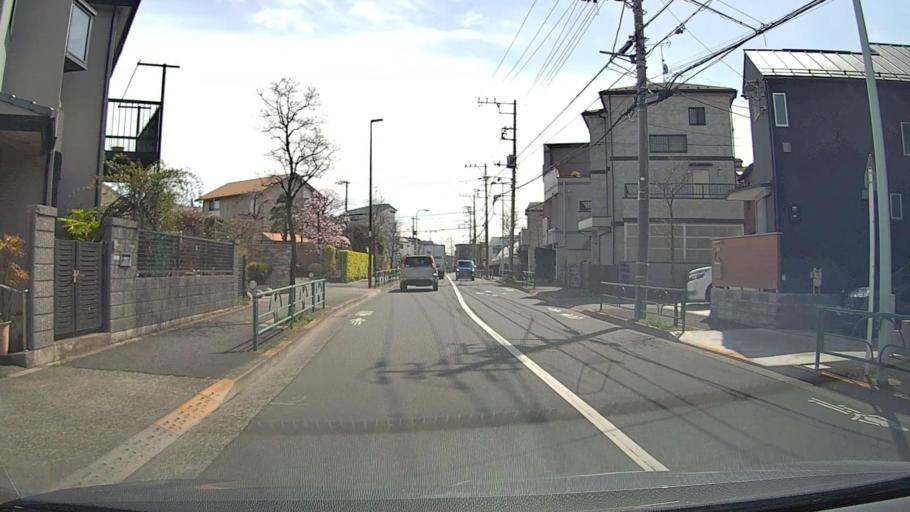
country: JP
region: Tokyo
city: Musashino
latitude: 35.7358
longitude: 139.5677
